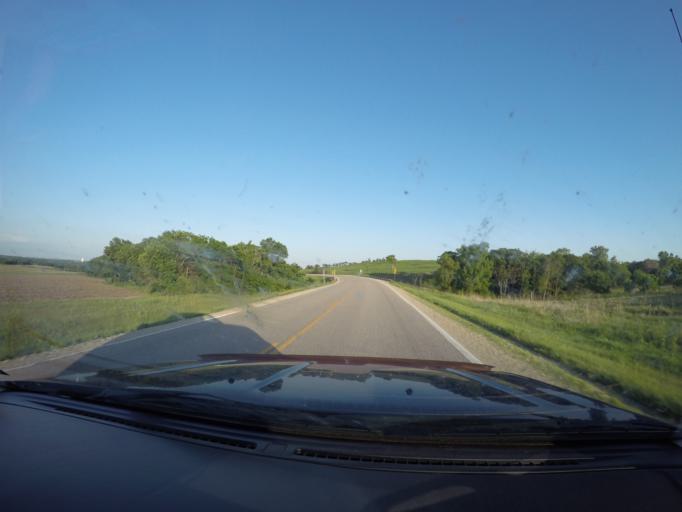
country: US
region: Kansas
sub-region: Marshall County
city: Blue Rapids
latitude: 39.6914
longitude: -96.7869
